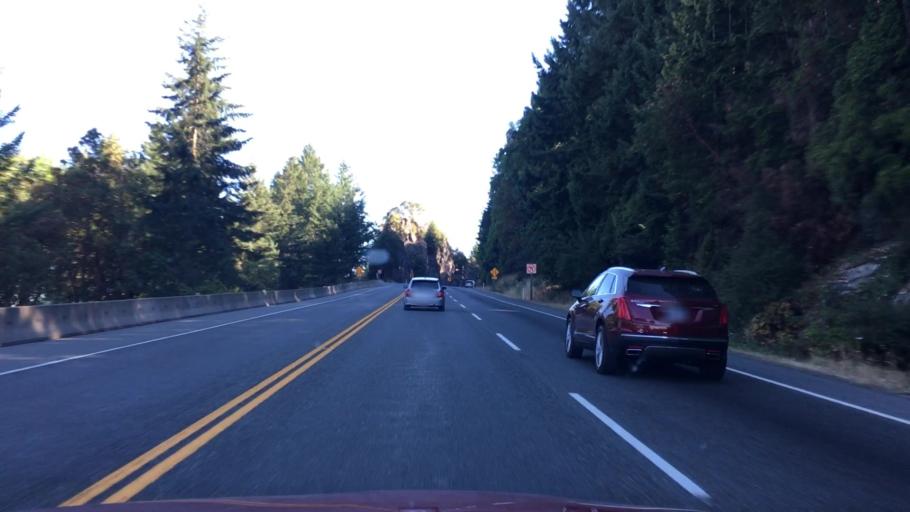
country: CA
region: British Columbia
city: North Saanich
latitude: 48.5865
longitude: -123.5308
